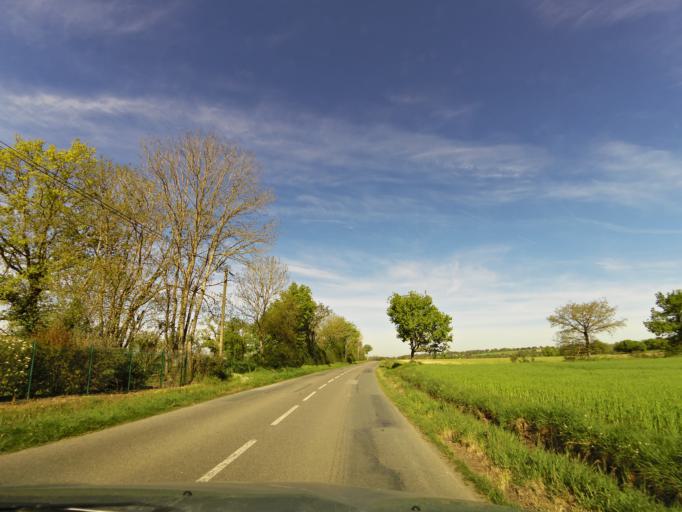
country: FR
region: Brittany
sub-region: Departement d'Ille-et-Vilaine
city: Pance
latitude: 47.8707
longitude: -1.6049
